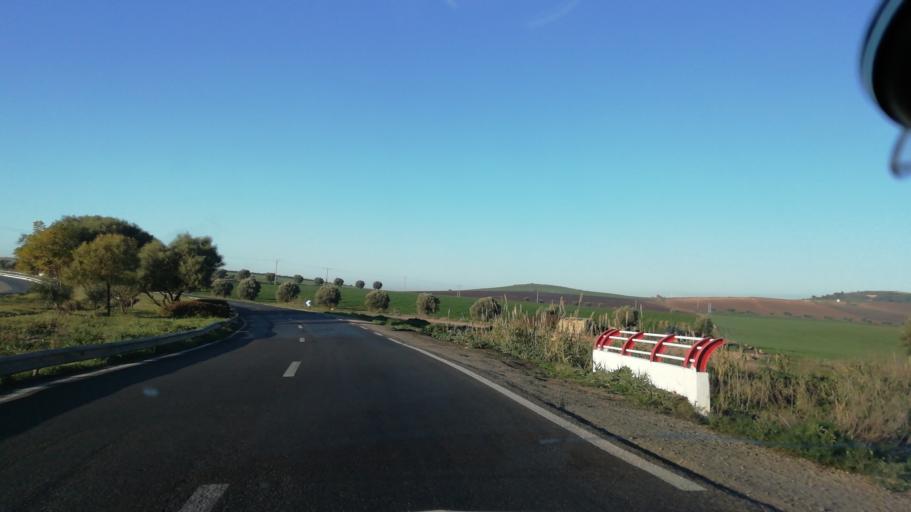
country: DZ
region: Ain Temouchent
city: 'Ain Temouchent
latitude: 35.2680
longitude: -1.2416
